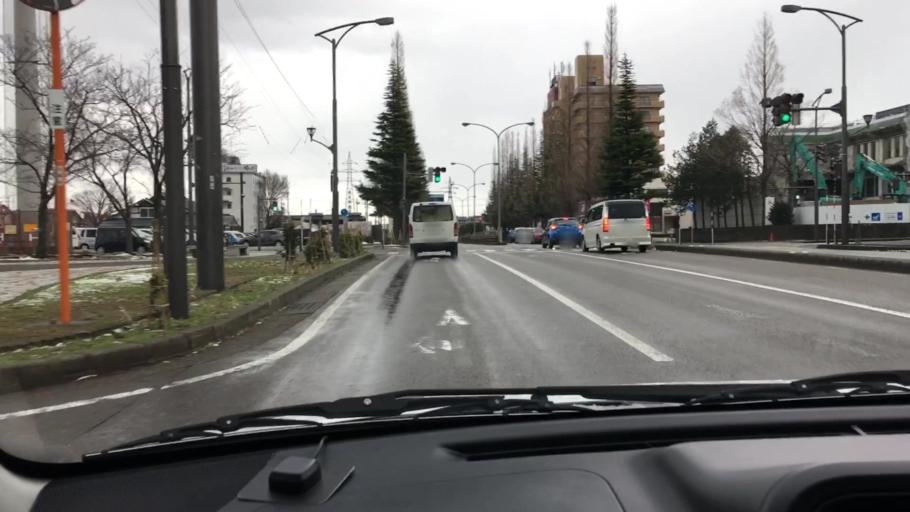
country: JP
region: Niigata
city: Joetsu
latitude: 37.1486
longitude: 138.2363
